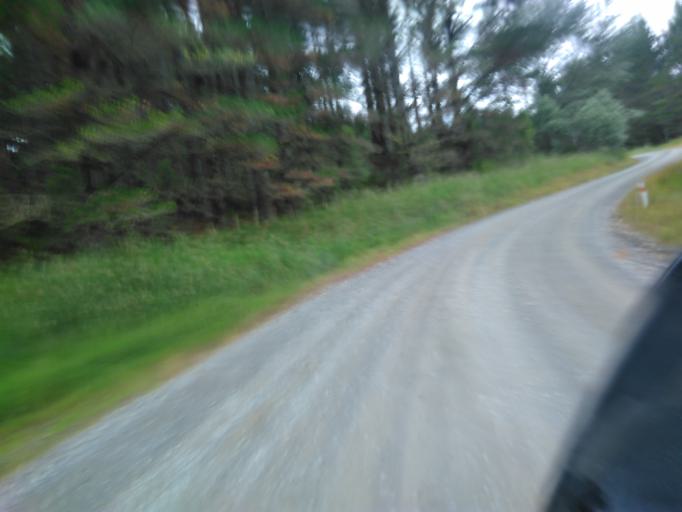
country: NZ
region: Gisborne
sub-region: Gisborne District
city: Gisborne
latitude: -38.0481
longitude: 178.1238
